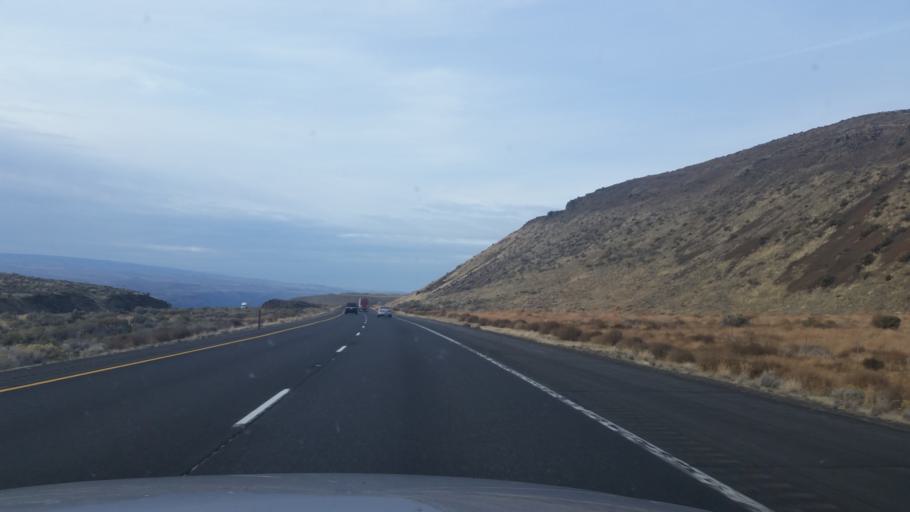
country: US
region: Washington
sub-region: Grant County
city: Mattawa
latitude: 46.9928
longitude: -119.9705
